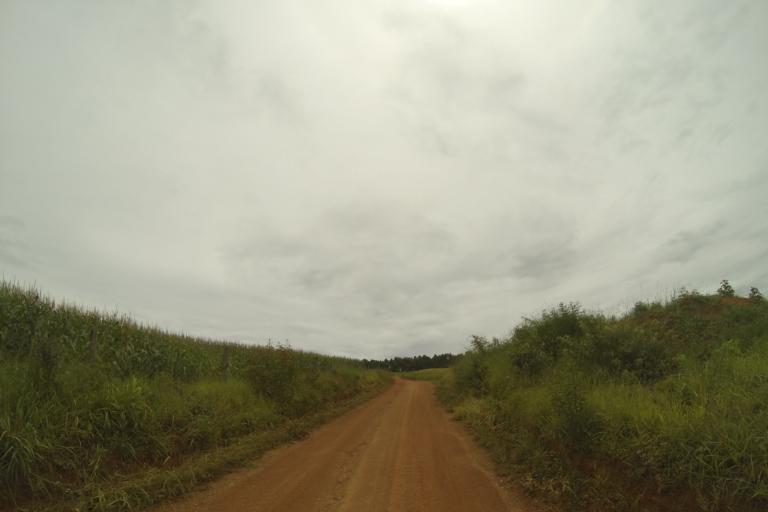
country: BR
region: Minas Gerais
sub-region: Ibia
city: Ibia
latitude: -19.7439
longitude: -46.6312
